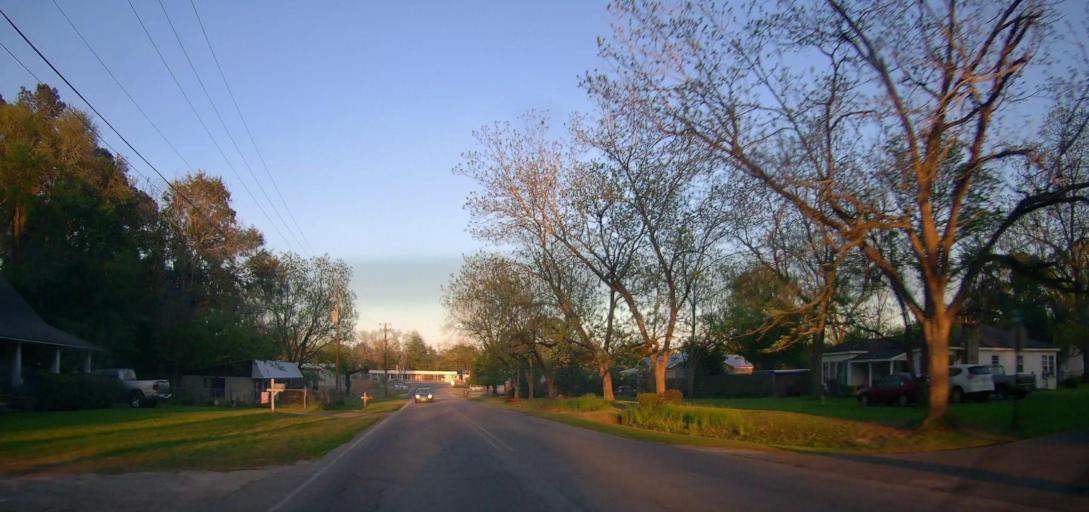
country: US
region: Georgia
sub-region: Ben Hill County
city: Fitzgerald
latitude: 31.7181
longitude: -83.2672
